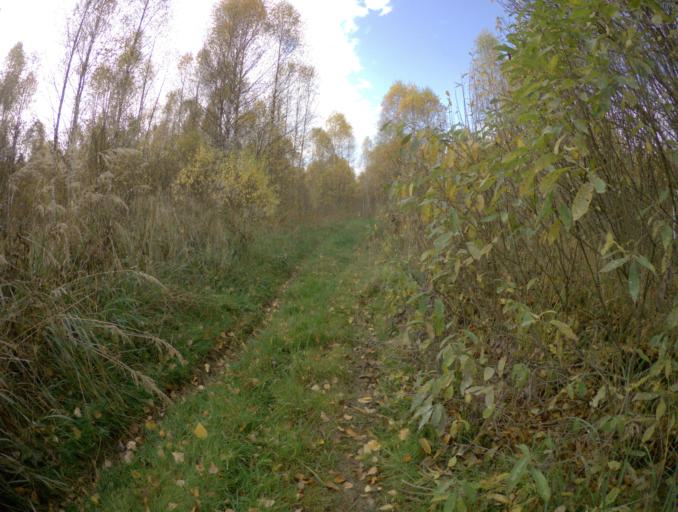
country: RU
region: Vladimir
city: Golovino
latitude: 55.9695
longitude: 40.3814
